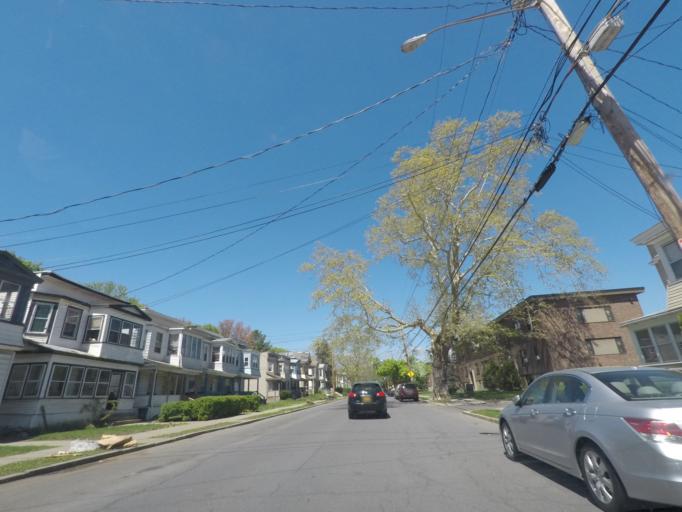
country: US
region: New York
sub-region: Albany County
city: Albany
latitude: 42.6670
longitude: -73.7642
